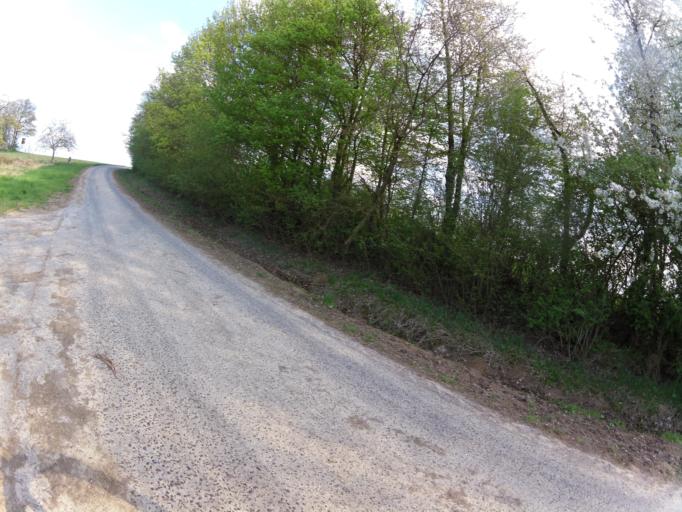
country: DE
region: Bavaria
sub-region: Regierungsbezirk Unterfranken
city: Winterhausen
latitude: 49.6936
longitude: 10.0092
